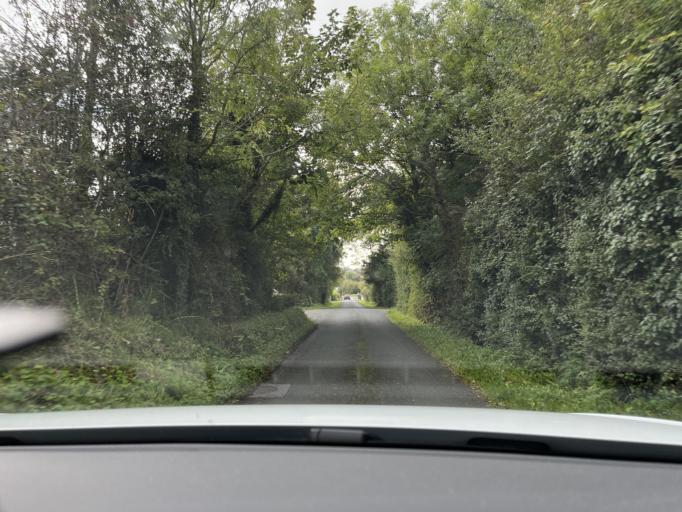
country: IE
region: Connaught
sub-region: County Leitrim
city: Carrick-on-Shannon
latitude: 53.9626
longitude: -8.0864
